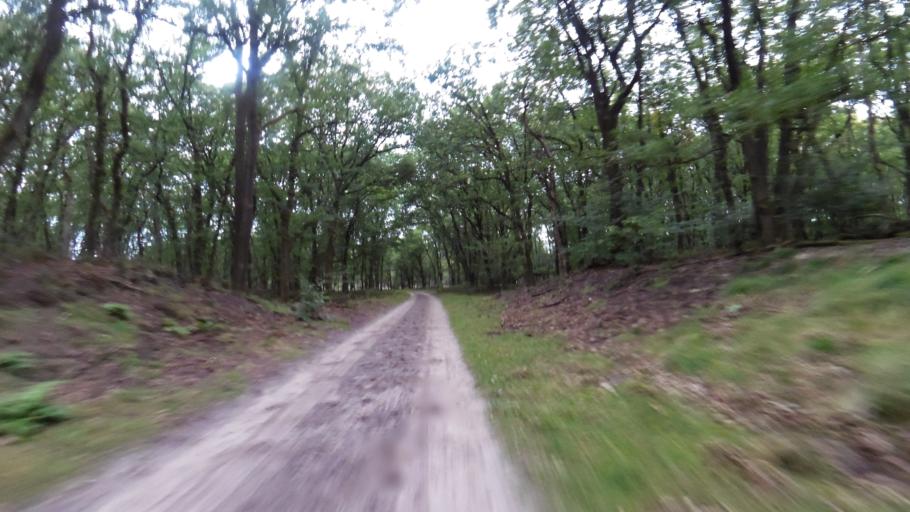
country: NL
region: Gelderland
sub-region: Gemeente Apeldoorn
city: Uddel
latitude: 52.1851
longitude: 5.8195
